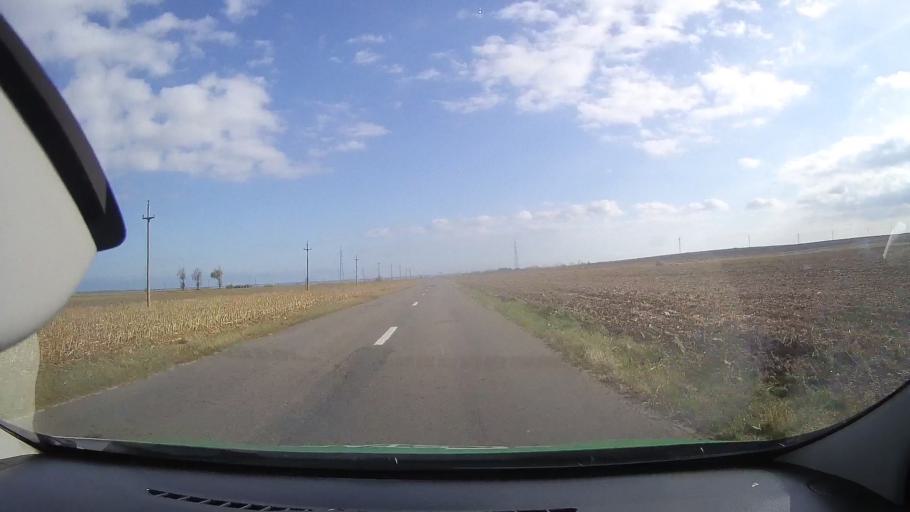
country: RO
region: Constanta
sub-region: Comuna Istria
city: Nuntasi
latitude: 44.5306
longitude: 28.6778
